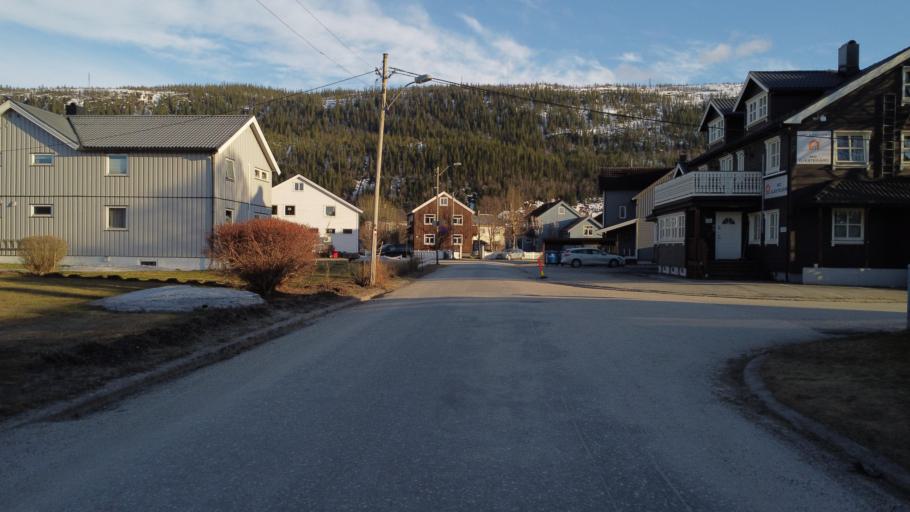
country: NO
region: Nordland
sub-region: Rana
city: Mo i Rana
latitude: 66.3089
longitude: 14.1427
